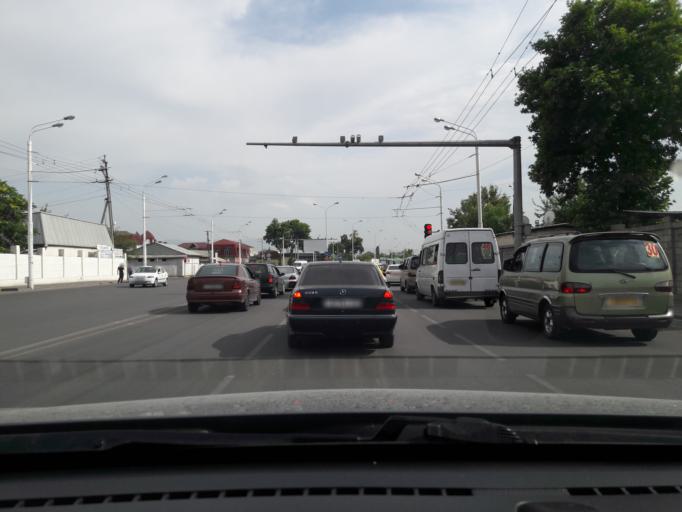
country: TJ
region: Dushanbe
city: Dushanbe
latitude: 38.5413
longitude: 68.7553
